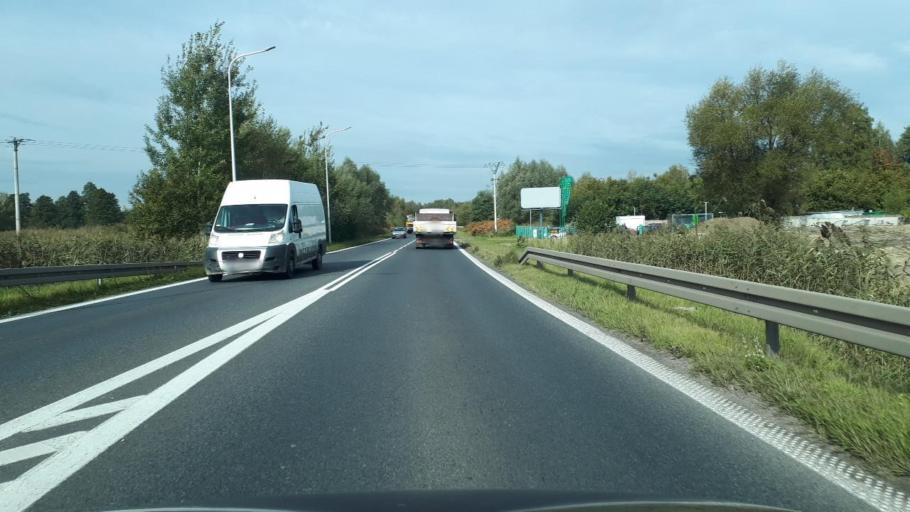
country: PL
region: Silesian Voivodeship
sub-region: Zory
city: Zory
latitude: 50.0544
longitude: 18.6990
